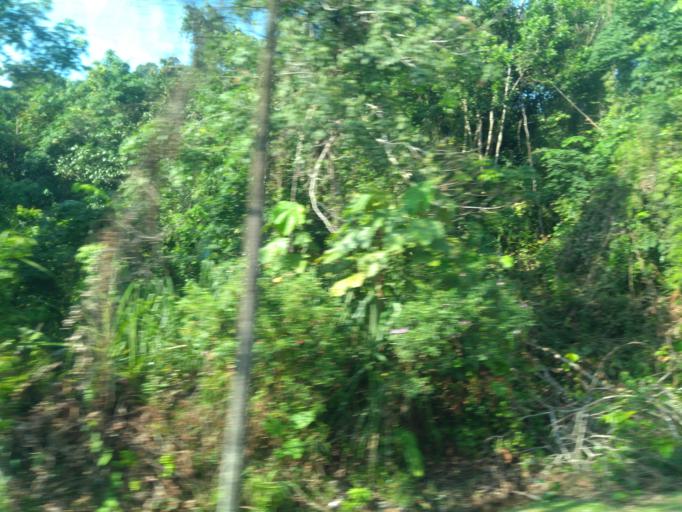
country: MY
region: Sarawak
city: Kuching
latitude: 1.6442
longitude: 110.4505
